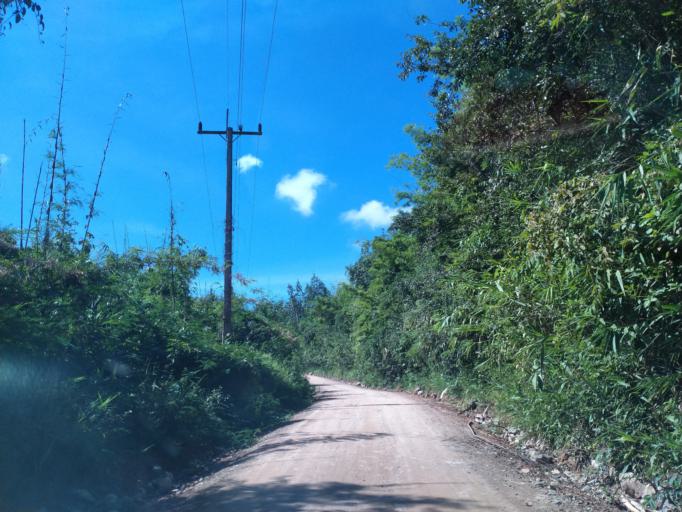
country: TH
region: Changwat Bueng Kan
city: Pak Khat
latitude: 18.6410
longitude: 103.0202
